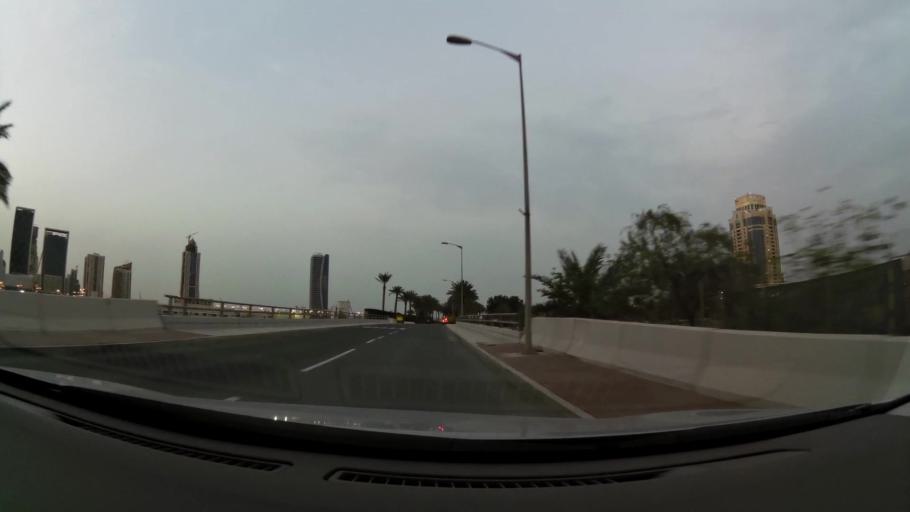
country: QA
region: Baladiyat ad Dawhah
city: Doha
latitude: 25.3783
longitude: 51.5272
